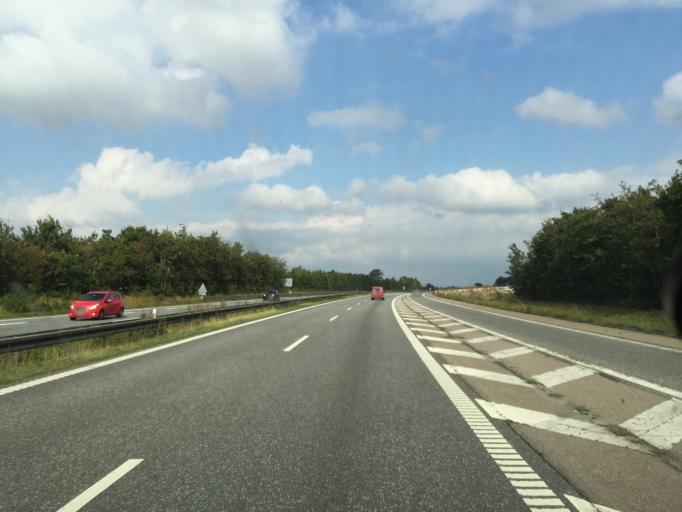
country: DK
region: Zealand
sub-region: Slagelse Kommune
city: Slagelse
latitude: 55.4213
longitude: 11.4168
